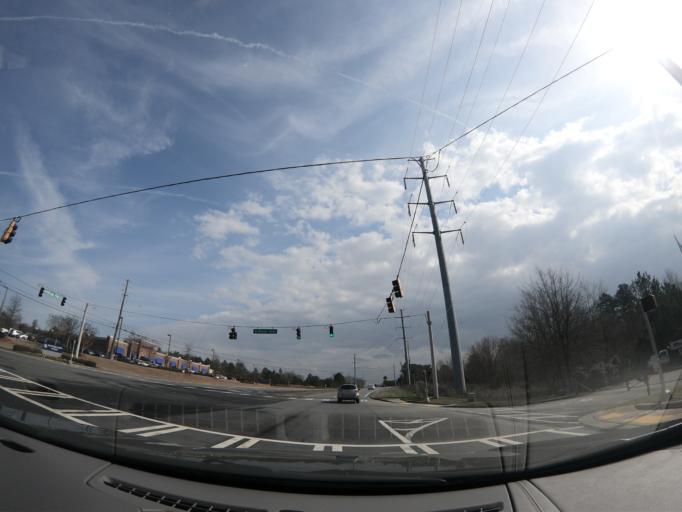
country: US
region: Georgia
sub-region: Fulton County
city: Milton
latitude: 34.1343
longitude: -84.2400
